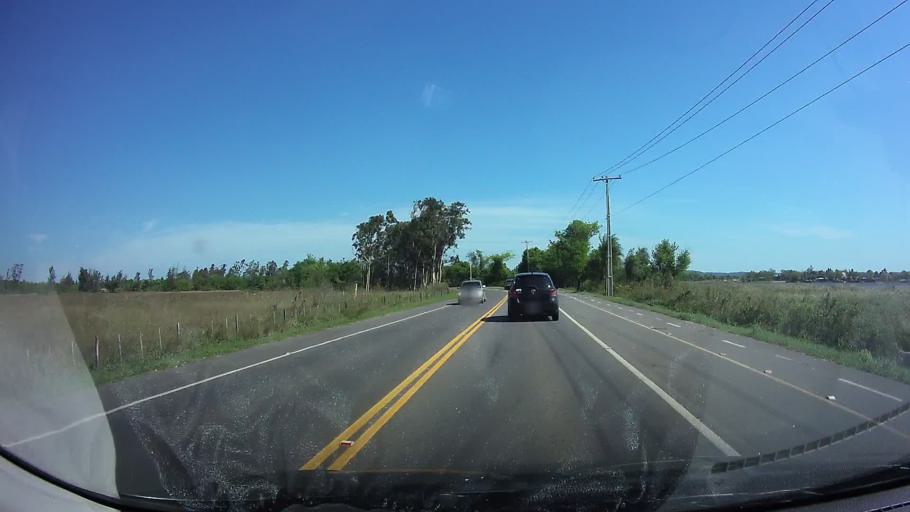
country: PY
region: Cordillera
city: San Bernardino
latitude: -25.2758
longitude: -57.3176
